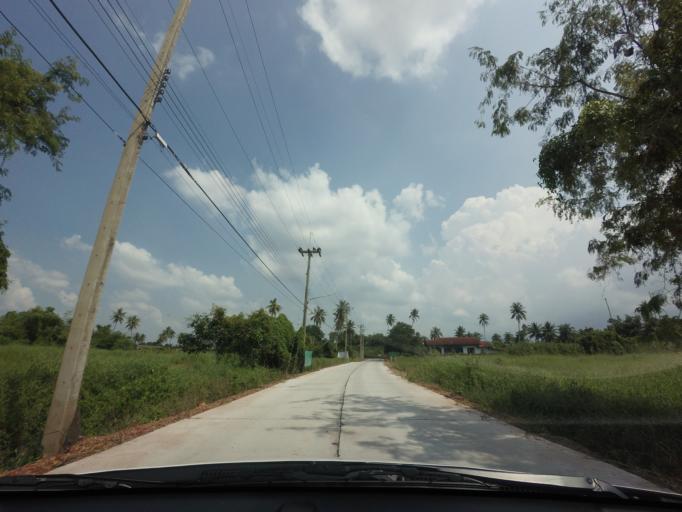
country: TH
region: Nakhon Pathom
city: Nakhon Chai Si
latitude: 13.8155
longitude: 100.1954
